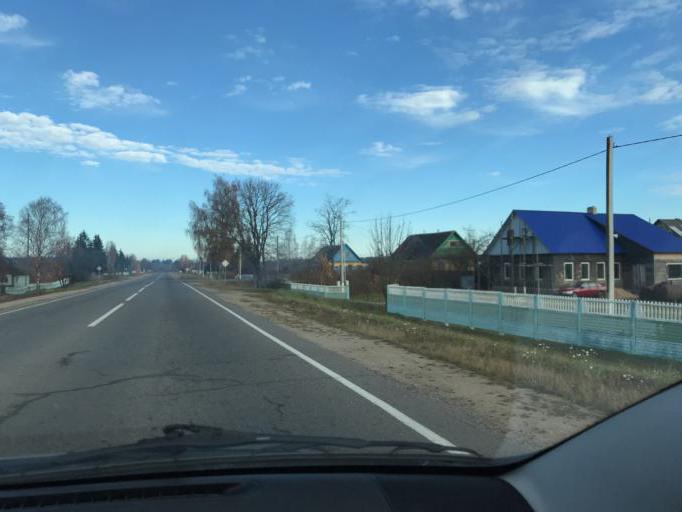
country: BY
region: Vitebsk
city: Haradok
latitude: 55.4865
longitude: 29.9677
